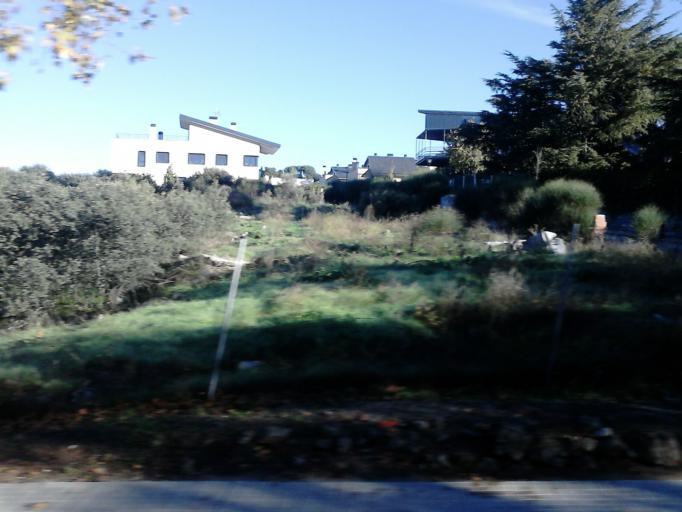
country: ES
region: Madrid
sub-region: Provincia de Madrid
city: Torrelodones
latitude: 40.5763
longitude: -3.9456
